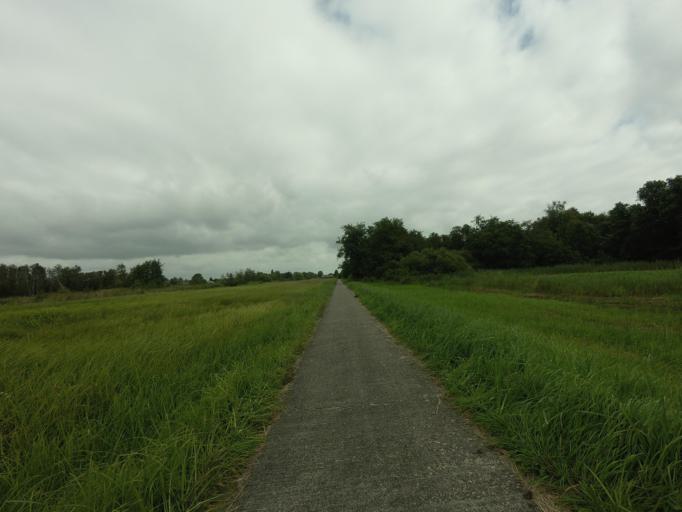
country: NL
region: Overijssel
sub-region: Gemeente Steenwijkerland
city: Sint Jansklooster
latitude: 52.7198
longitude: 6.0300
